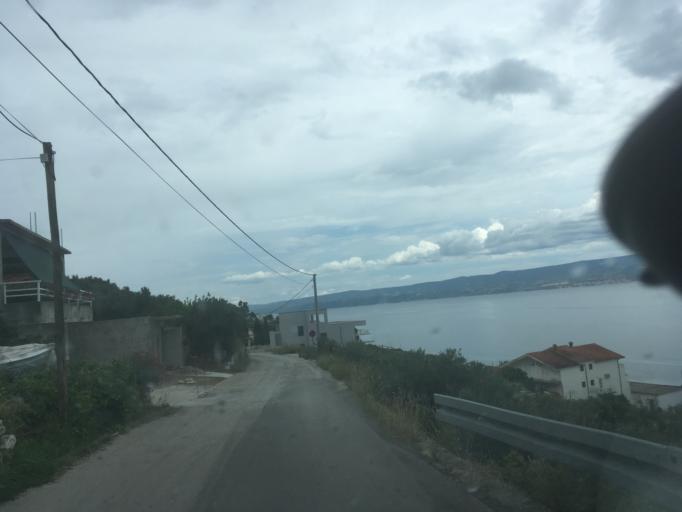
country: HR
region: Splitsko-Dalmatinska
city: Jesenice
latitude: 43.4564
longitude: 16.6214
